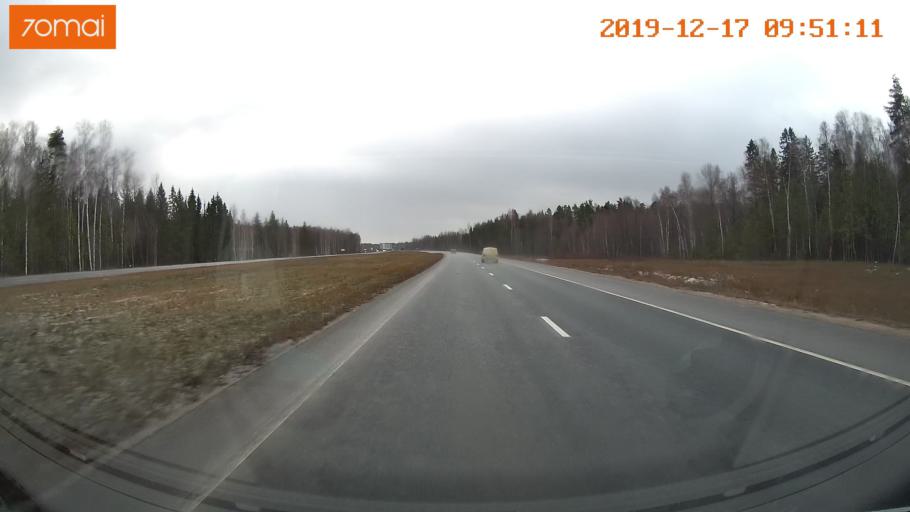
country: RU
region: Vladimir
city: Kommunar
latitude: 56.0473
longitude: 40.5178
